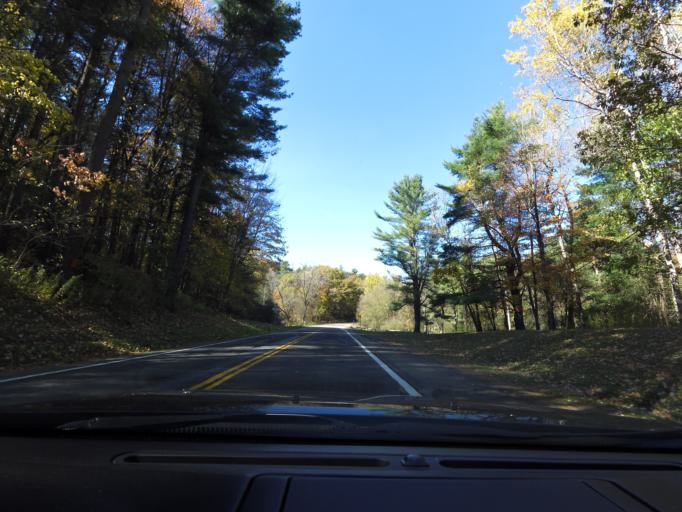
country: US
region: New York
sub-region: Wyoming County
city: Castile
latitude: 42.5707
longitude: -78.0532
